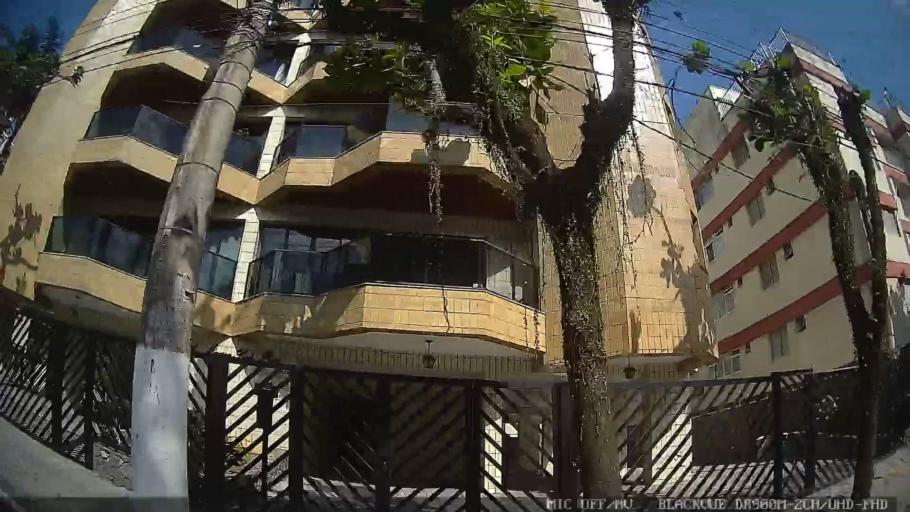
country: BR
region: Sao Paulo
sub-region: Guaruja
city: Guaruja
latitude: -23.9840
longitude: -46.2036
